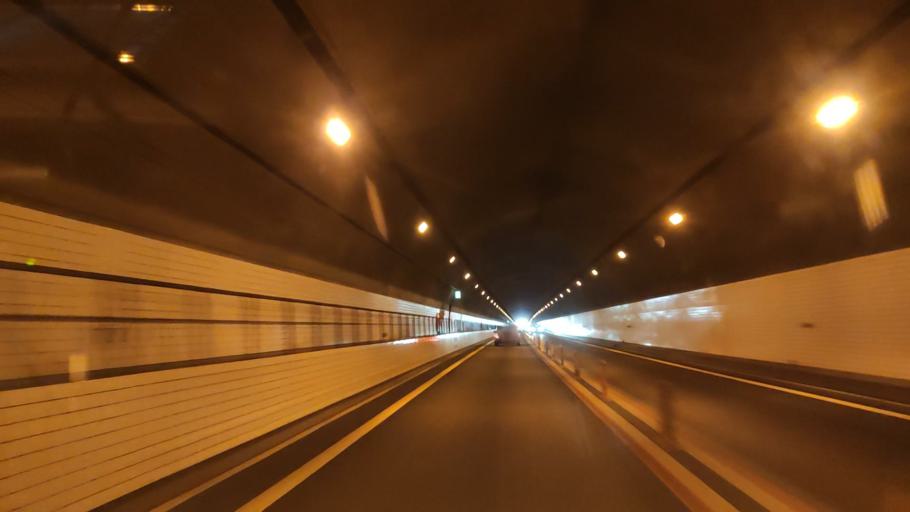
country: JP
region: Tokushima
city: Ikedacho
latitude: 34.0211
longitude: 133.8057
